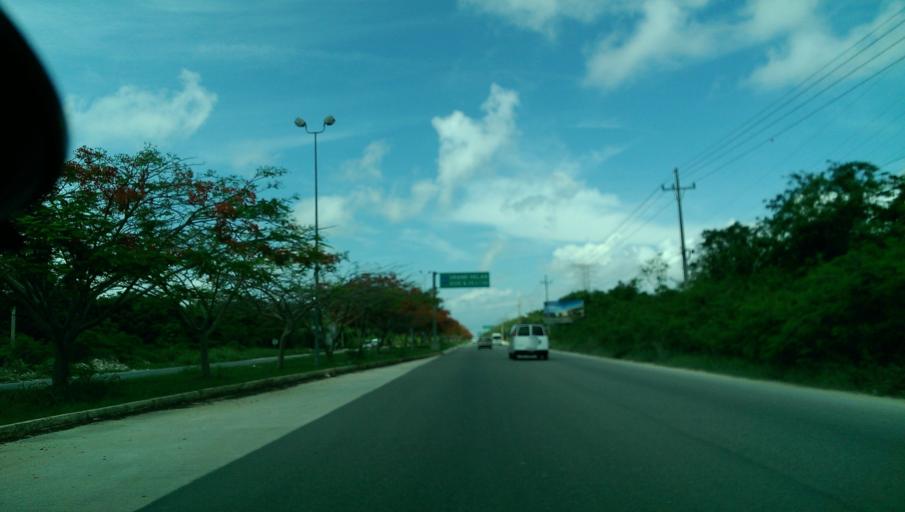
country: MX
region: Quintana Roo
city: Playa del Carmen
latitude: 20.6980
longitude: -87.0298
